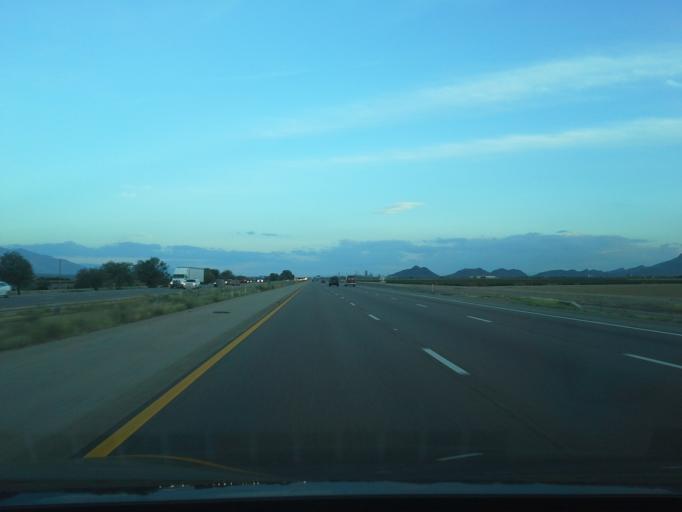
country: US
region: Arizona
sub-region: Pima County
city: Marana
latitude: 32.4453
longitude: -111.1929
